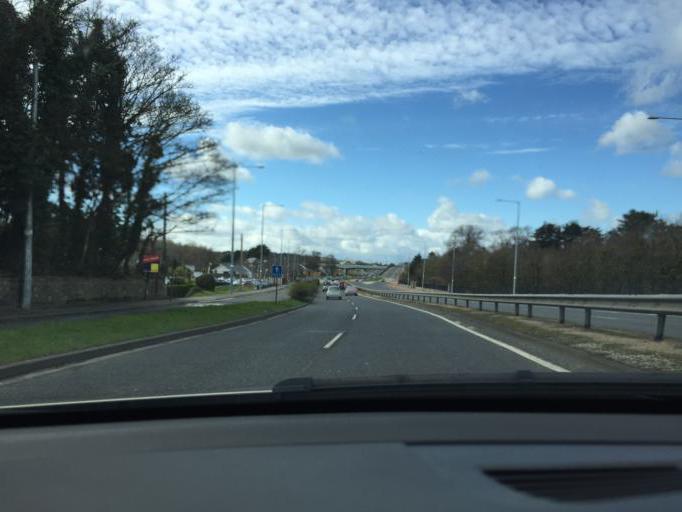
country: IE
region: Leinster
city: Loughlinstown
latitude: 53.2435
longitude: -6.1315
